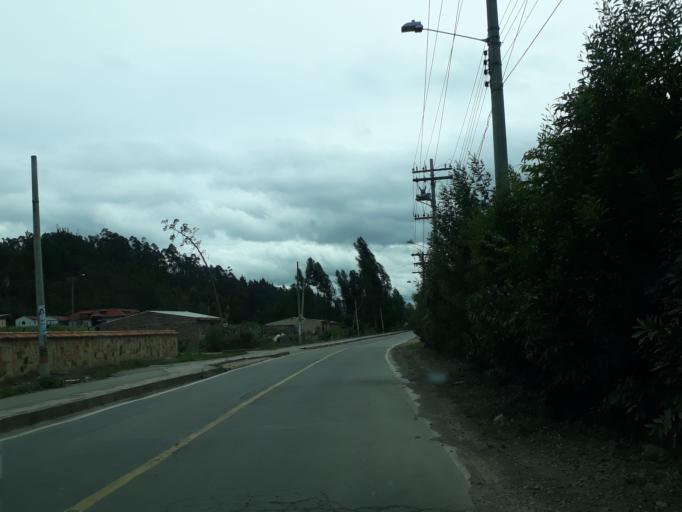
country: CO
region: Cundinamarca
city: Simijaca
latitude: 5.5141
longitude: -73.8417
